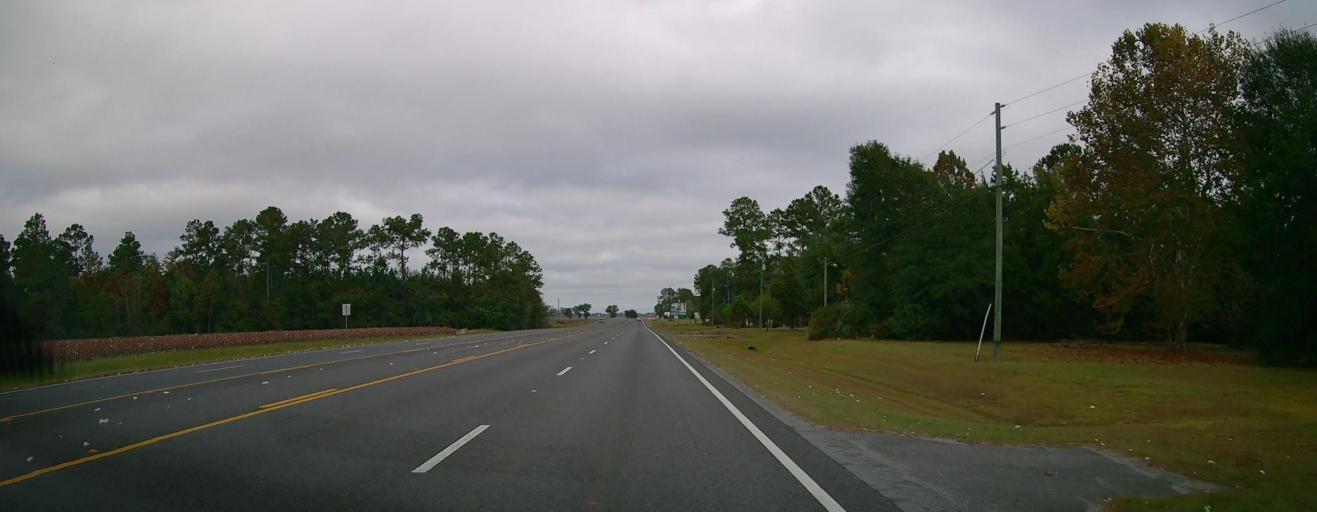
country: US
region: Georgia
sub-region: Colquitt County
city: Moultrie
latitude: 31.0208
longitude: -83.8637
